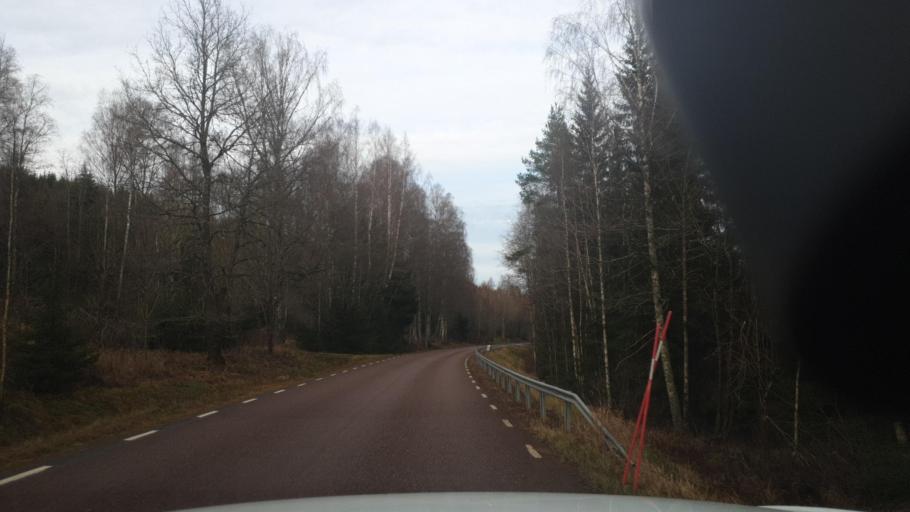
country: NO
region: Hedmark
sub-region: Eidskog
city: Skotterud
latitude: 59.7637
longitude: 12.0490
